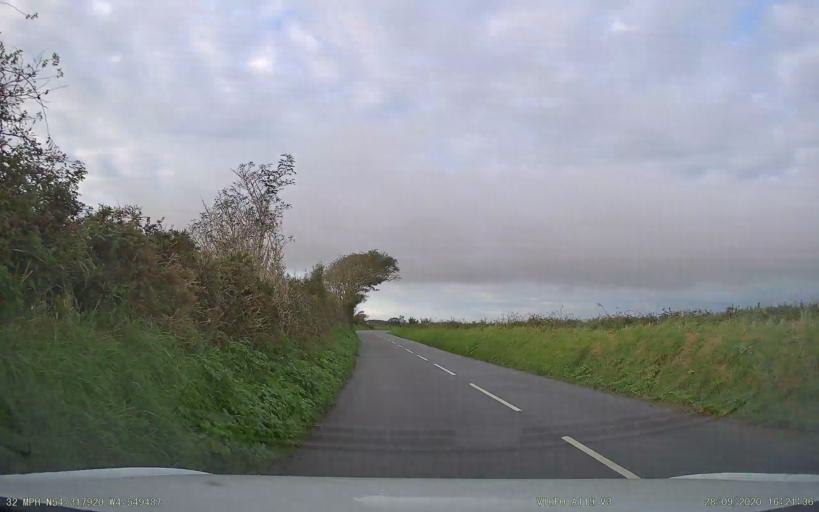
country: IM
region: Ramsey
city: Ramsey
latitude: 54.3179
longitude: -4.5495
